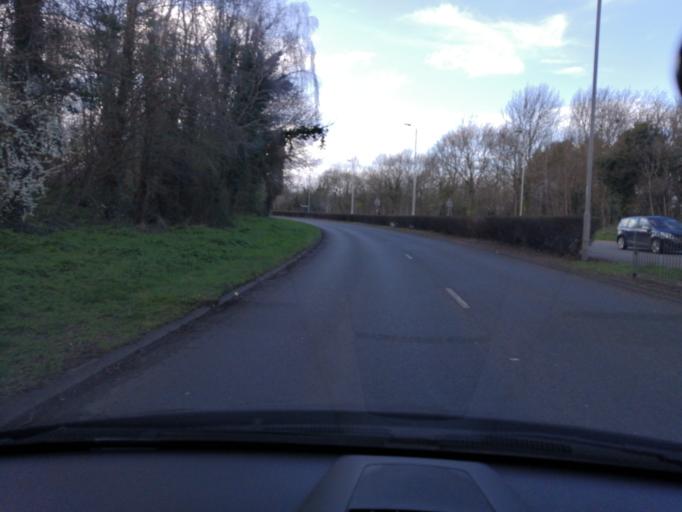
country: GB
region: England
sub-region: Peterborough
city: Marholm
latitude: 52.6045
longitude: -0.2775
